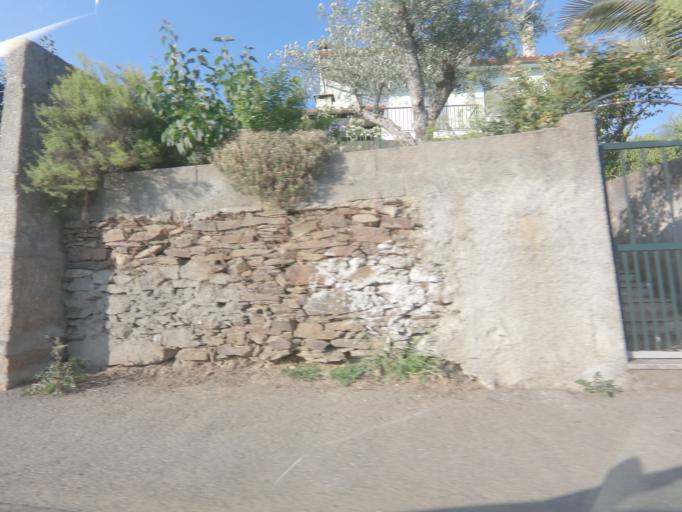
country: PT
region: Vila Real
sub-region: Sabrosa
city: Vilela
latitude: 41.2694
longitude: -7.6633
